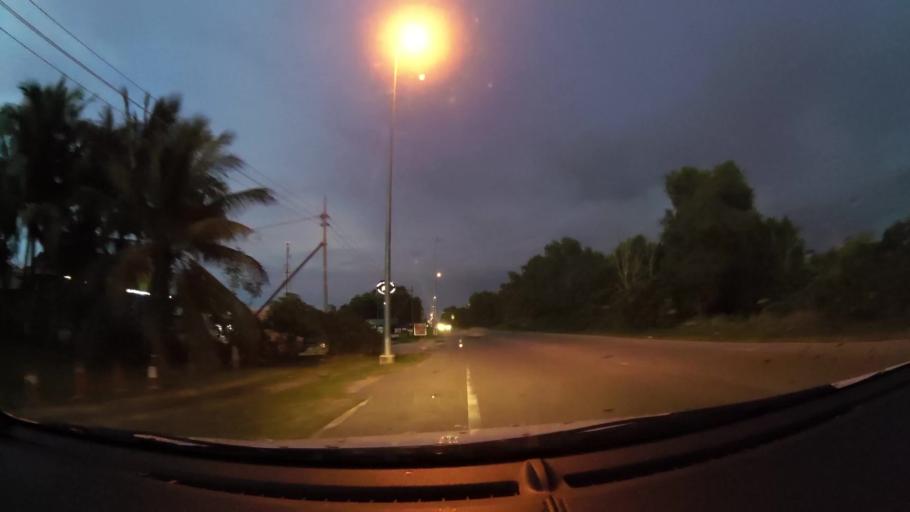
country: BN
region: Belait
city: Seria
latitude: 4.6530
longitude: 114.4276
